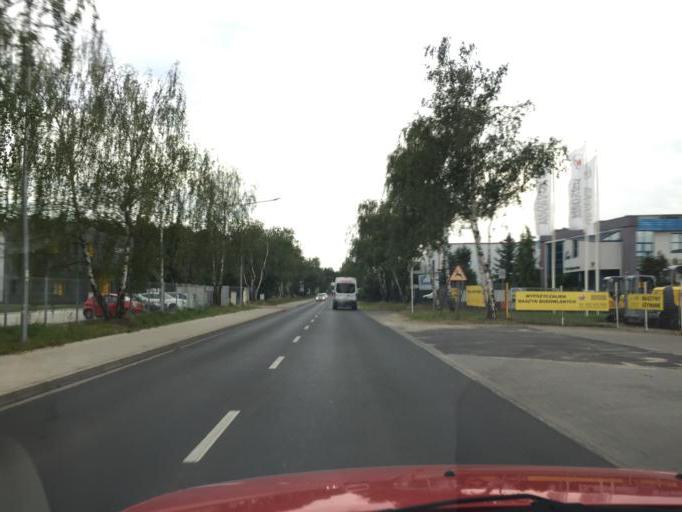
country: PL
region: Greater Poland Voivodeship
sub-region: Powiat poznanski
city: Baranowo
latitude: 52.4082
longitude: 16.7935
